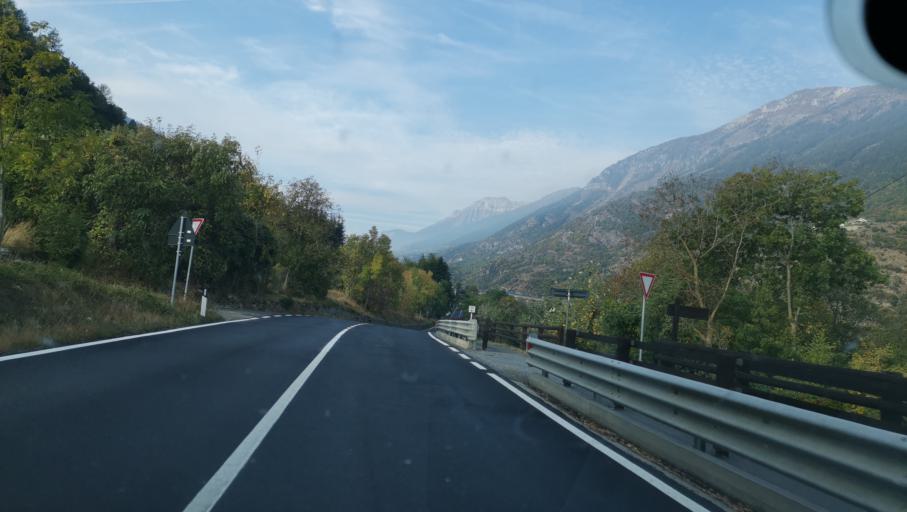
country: IT
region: Piedmont
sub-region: Provincia di Torino
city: Chiomonte
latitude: 45.1235
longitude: 6.9965
